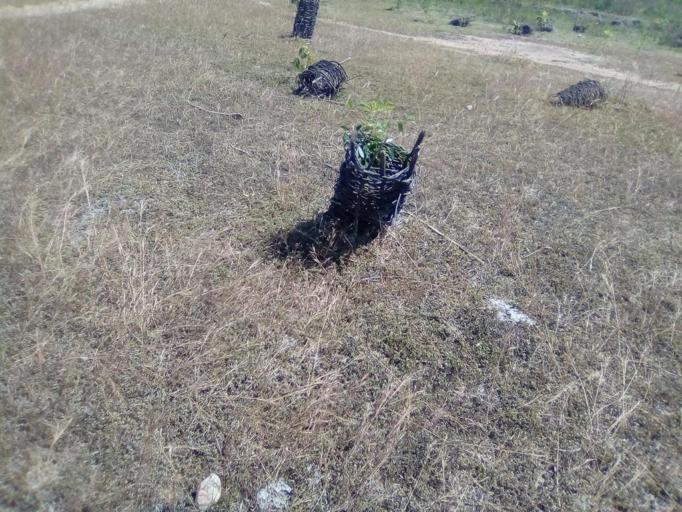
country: GH
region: Upper East
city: Bawku
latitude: 11.0942
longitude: -0.0722
